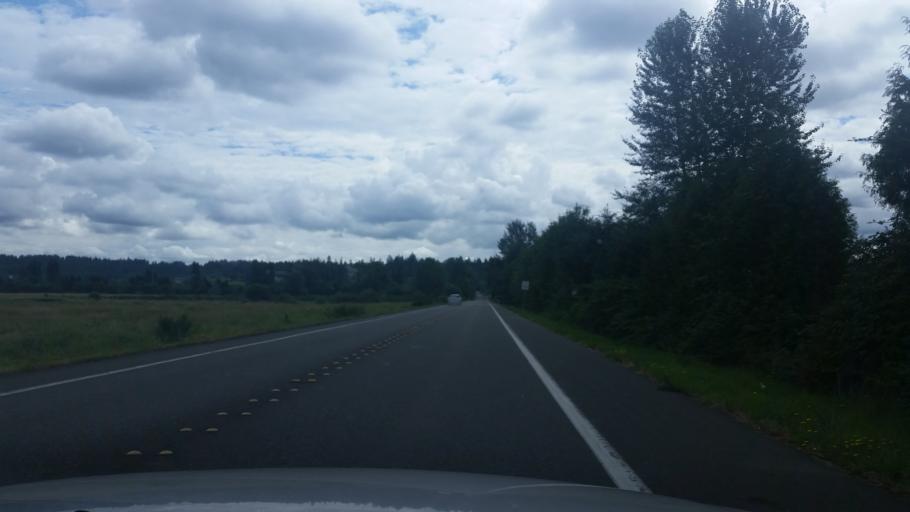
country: US
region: Washington
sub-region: King County
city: Kingsgate
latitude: 47.7043
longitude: -122.1515
